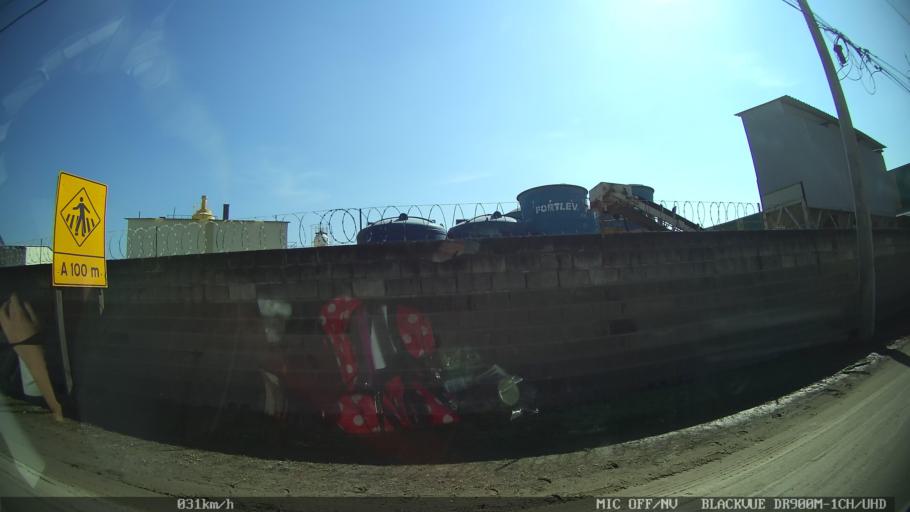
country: BR
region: Sao Paulo
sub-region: Valinhos
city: Valinhos
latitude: -23.0004
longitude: -47.0878
